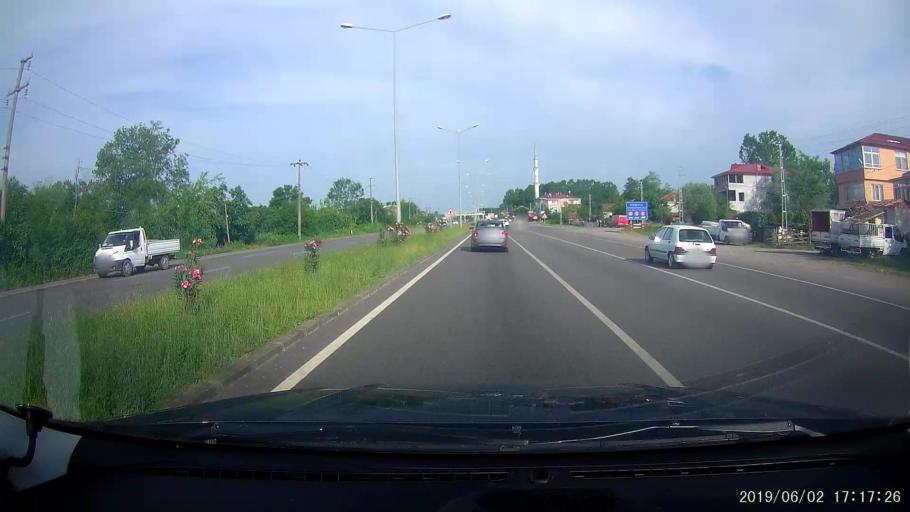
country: TR
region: Samsun
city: Dikbiyik
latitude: 41.2289
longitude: 36.5816
